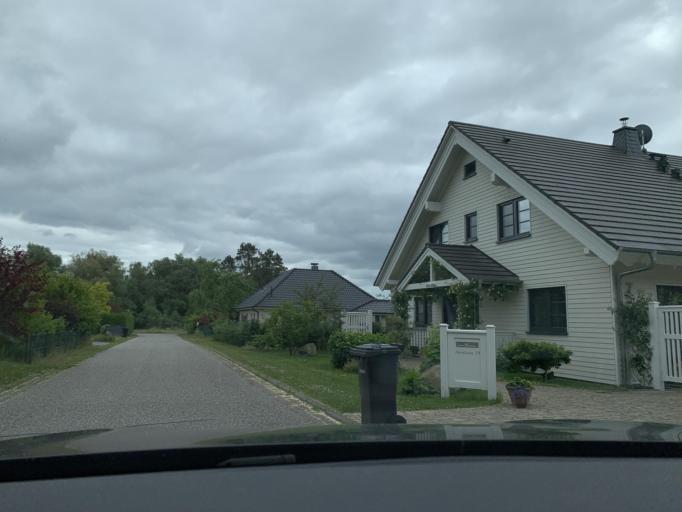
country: DE
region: Mecklenburg-Vorpommern
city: Rechlin
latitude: 53.3519
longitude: 12.7202
